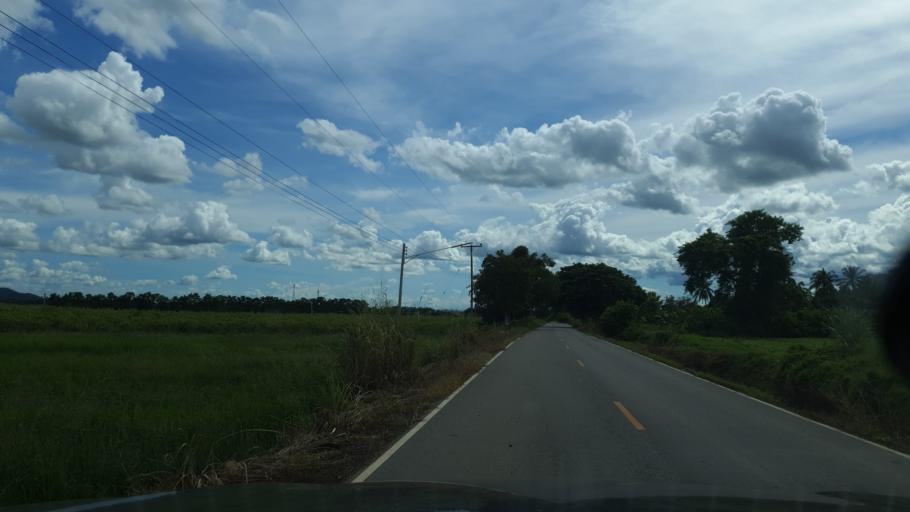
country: TH
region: Sukhothai
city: Thung Saliam
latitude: 17.3424
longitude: 99.6372
